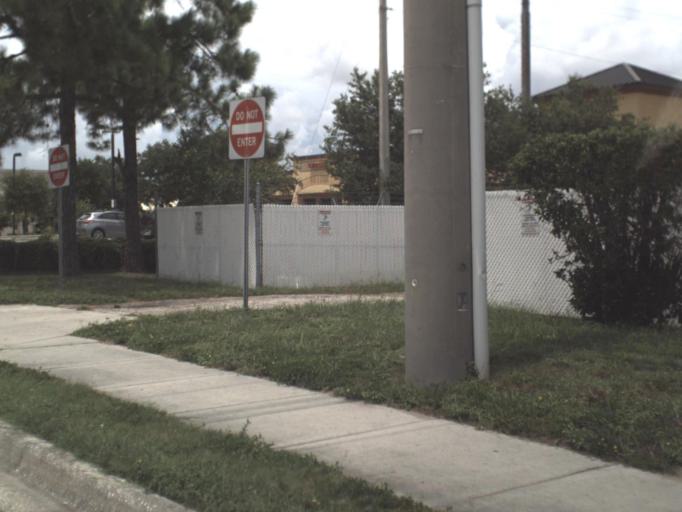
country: US
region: Florida
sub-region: Pinellas County
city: Saint George
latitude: 28.0491
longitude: -82.6965
